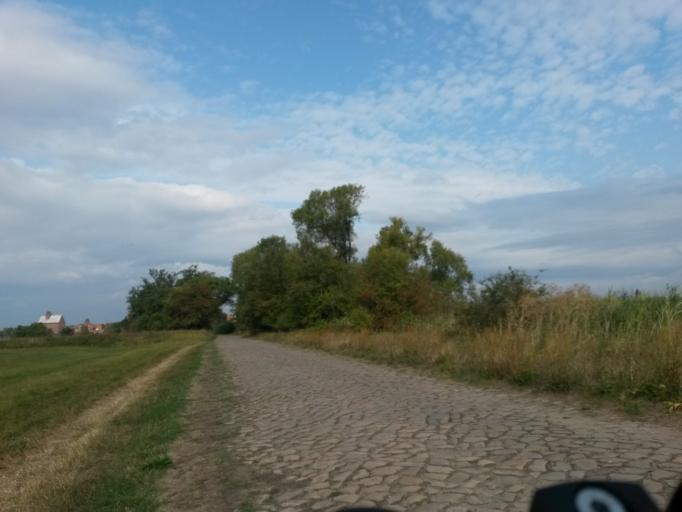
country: DE
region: Saxony-Anhalt
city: Tangermunde
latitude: 52.5370
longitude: 11.9885
